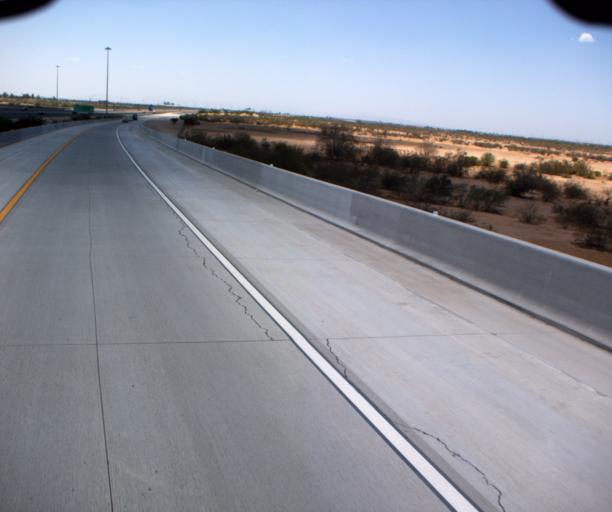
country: US
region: Arizona
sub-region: Maricopa County
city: Queen Creek
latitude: 33.3304
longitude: -111.6576
